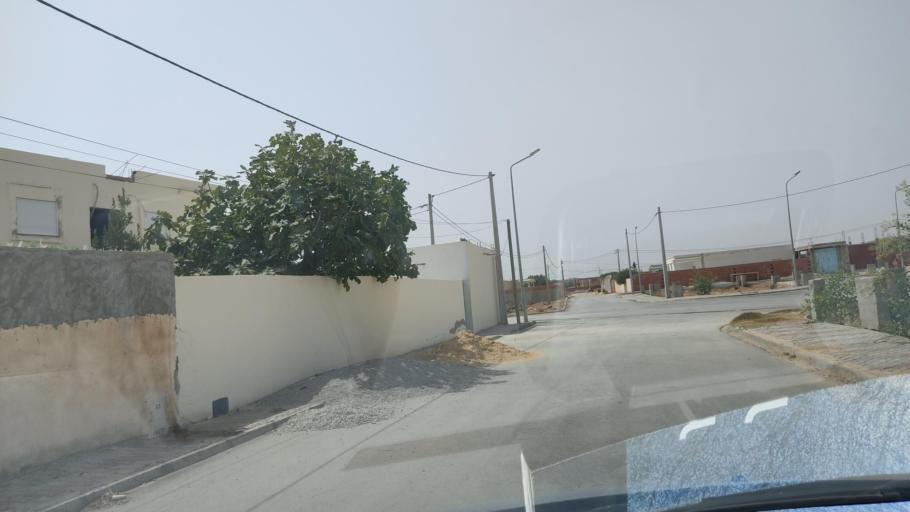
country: TN
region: Al Mahdiyah
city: El Jem
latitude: 35.1270
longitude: 10.7365
